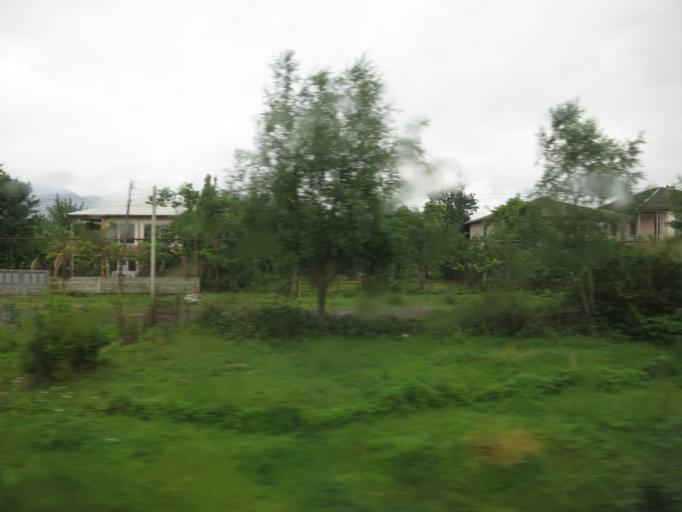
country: GE
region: Guria
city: Lanchkhuti
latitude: 42.0954
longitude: 42.0321
